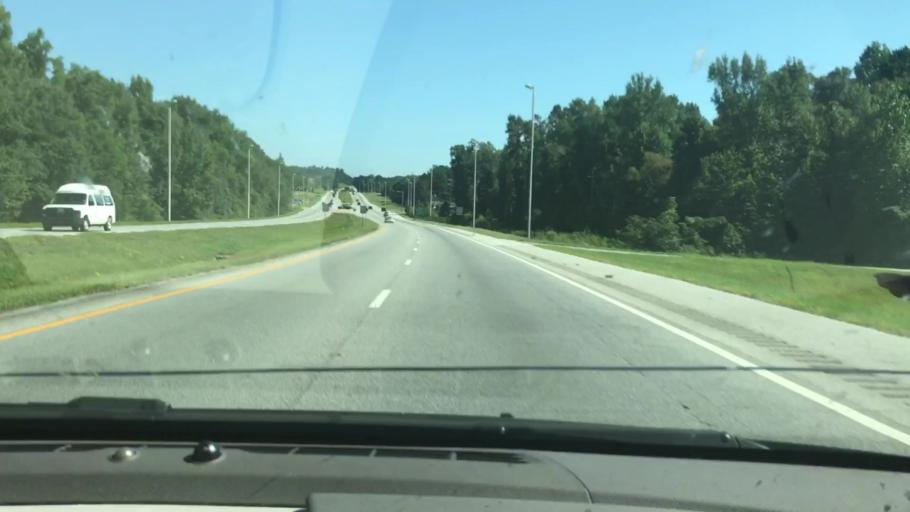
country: US
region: Alabama
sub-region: Russell County
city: Phenix City
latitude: 32.4341
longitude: -85.0256
